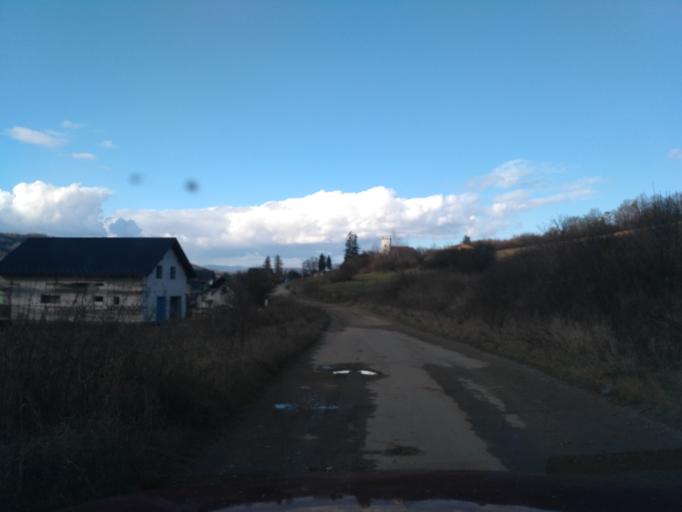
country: SK
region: Presovsky
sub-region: Okres Presov
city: Presov
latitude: 48.9301
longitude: 21.1940
